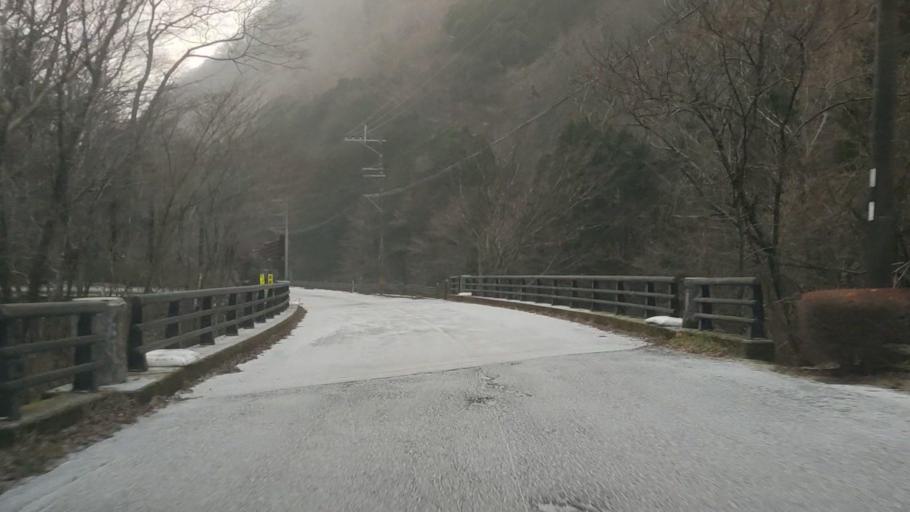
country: JP
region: Kumamoto
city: Matsubase
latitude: 32.5557
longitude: 130.9224
